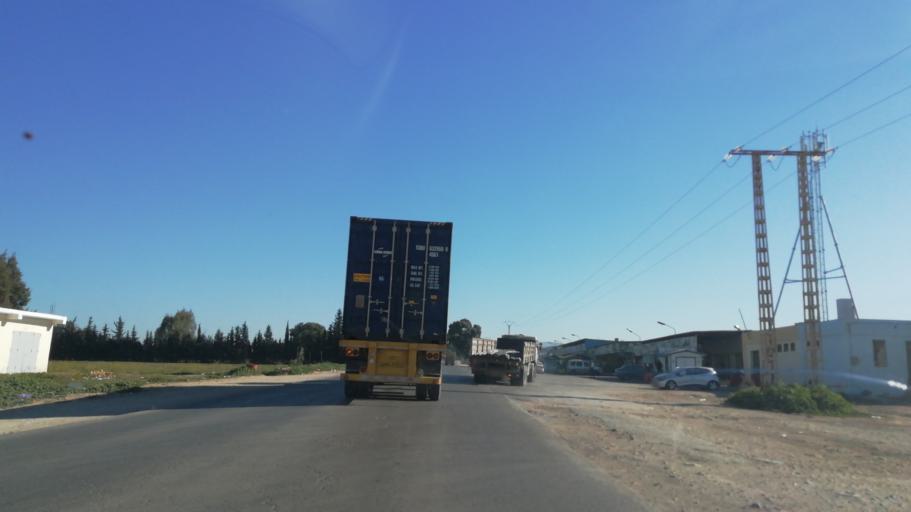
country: DZ
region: Relizane
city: Zemoura
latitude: 35.7427
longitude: 0.7033
